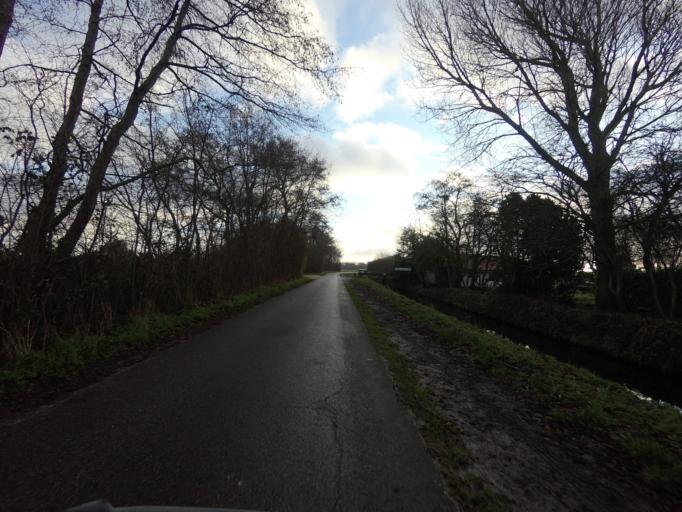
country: NL
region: North Holland
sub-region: Gemeente Texel
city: Den Burg
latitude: 53.0934
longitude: 4.7750
